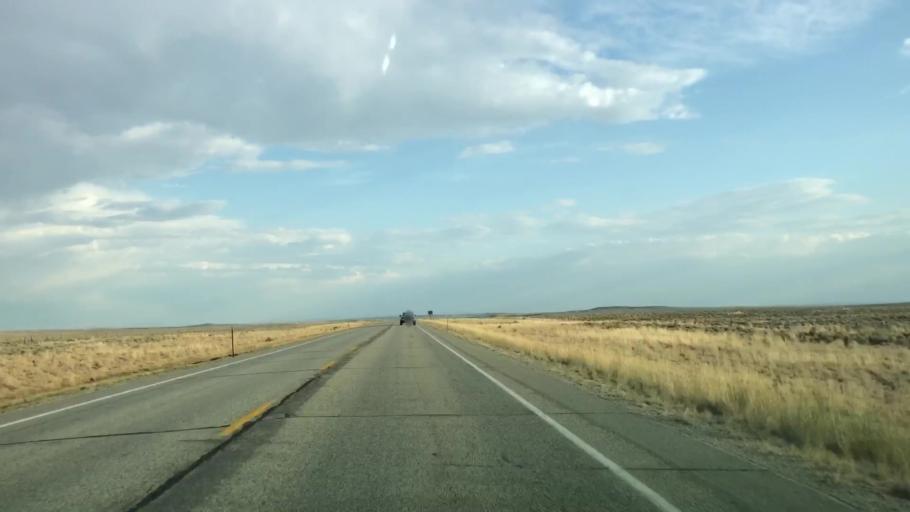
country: US
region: Wyoming
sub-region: Sublette County
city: Pinedale
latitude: 42.3943
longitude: -109.5426
